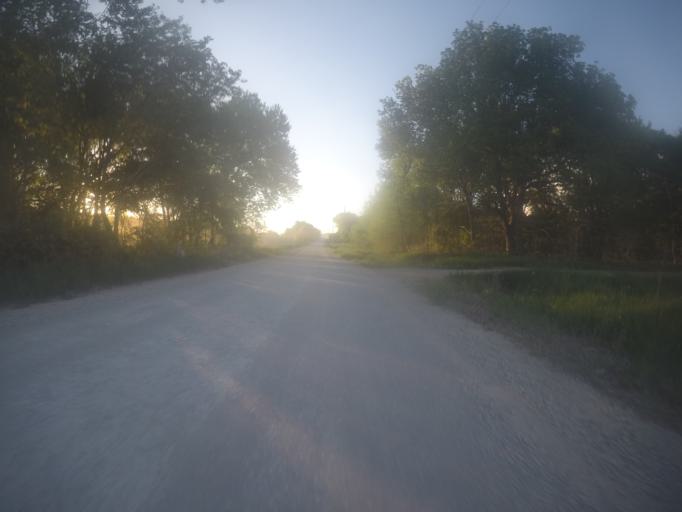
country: US
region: Kansas
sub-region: Riley County
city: Manhattan
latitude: 39.2343
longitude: -96.5551
